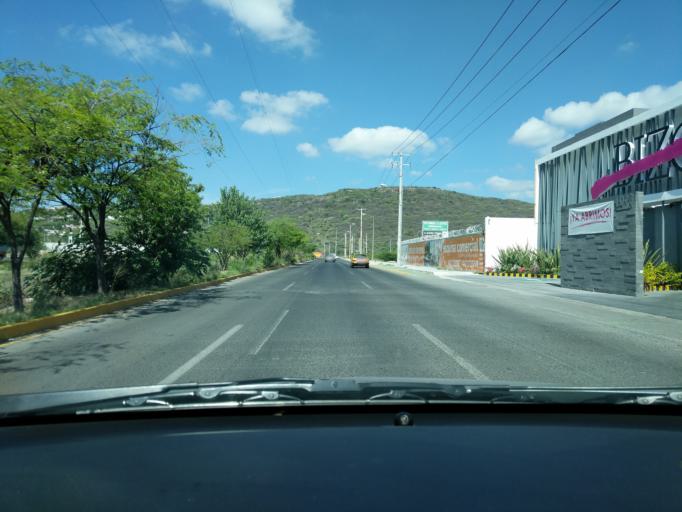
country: MX
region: Queretaro
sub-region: Queretaro
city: Patria Nueva
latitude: 20.6402
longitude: -100.4977
